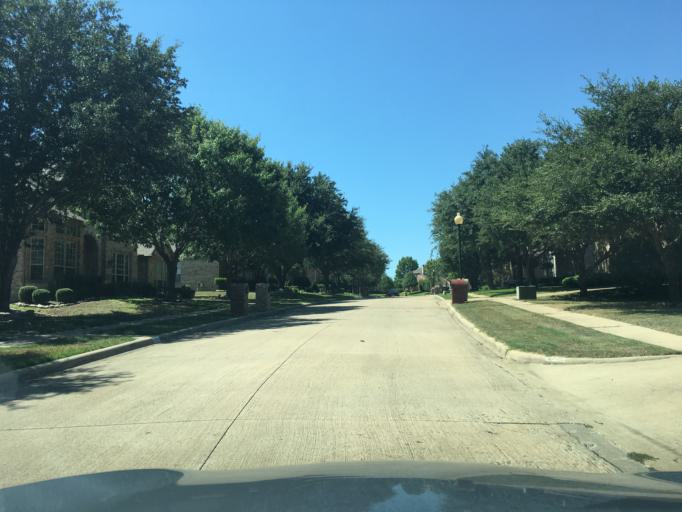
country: US
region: Texas
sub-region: Dallas County
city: Sachse
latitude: 32.9615
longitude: -96.6218
